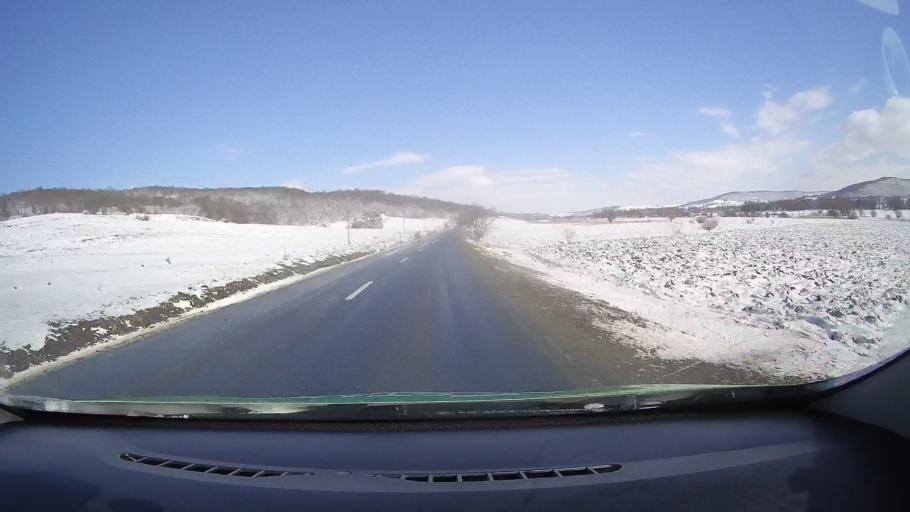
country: RO
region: Sibiu
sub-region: Comuna Rosia
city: Rosia
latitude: 45.8247
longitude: 24.3854
